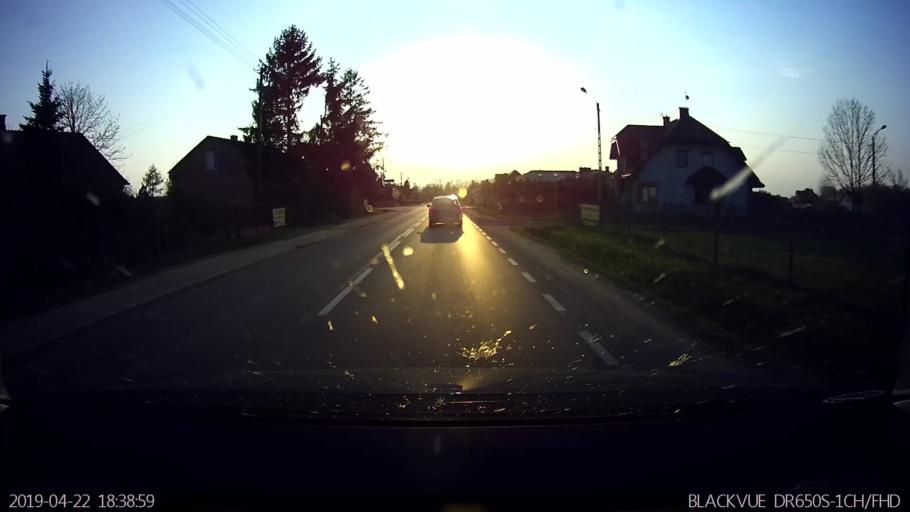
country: PL
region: Masovian Voivodeship
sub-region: Powiat wolominski
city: Dabrowka
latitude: 52.4415
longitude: 21.2905
